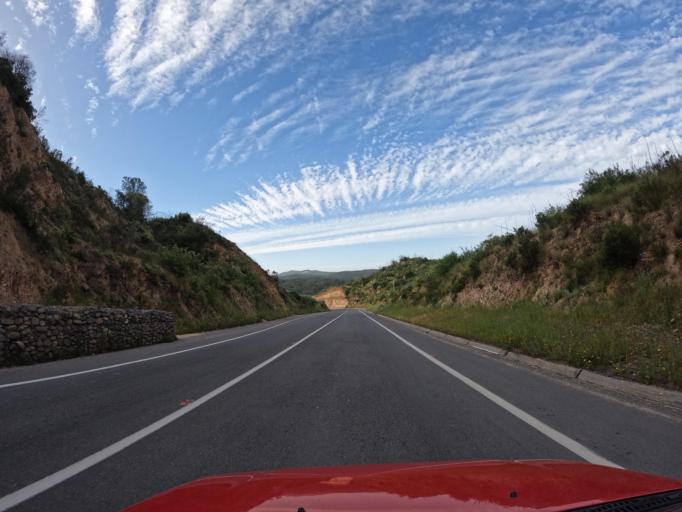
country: CL
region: Valparaiso
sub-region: San Antonio Province
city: San Antonio
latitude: -34.0445
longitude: -71.5929
